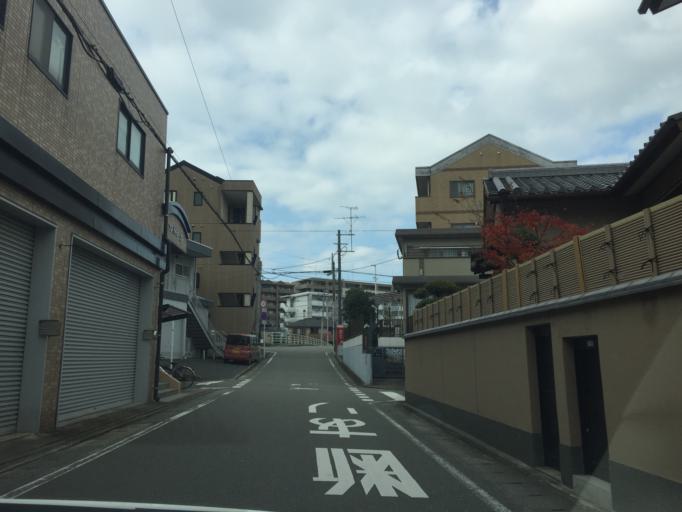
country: JP
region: Fukuoka
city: Fukuoka-shi
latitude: 33.6143
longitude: 130.4279
